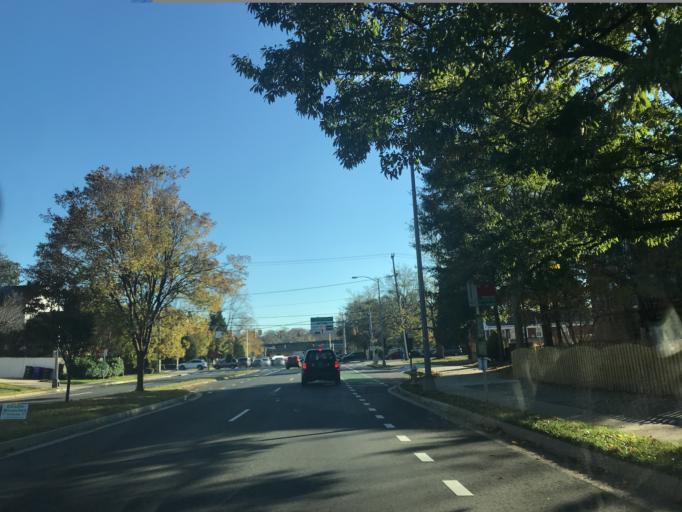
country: US
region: Virginia
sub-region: City of Falls Church
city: Falls Church
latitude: 38.8884
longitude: -77.1564
